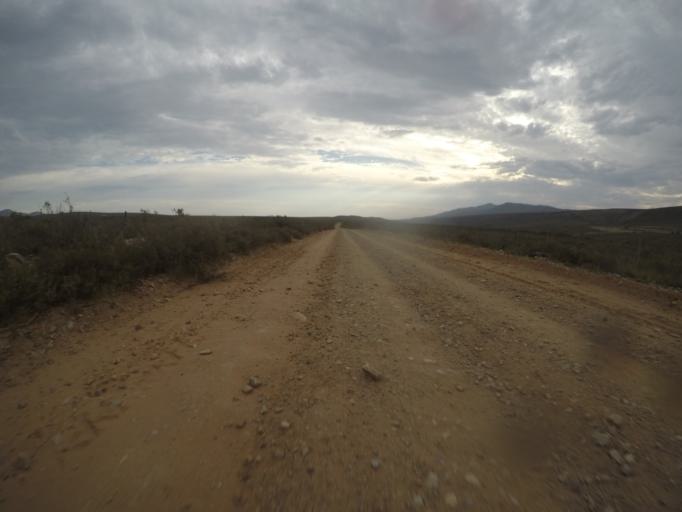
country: ZA
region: Eastern Cape
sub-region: Cacadu District Municipality
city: Willowmore
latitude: -33.4921
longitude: 23.5844
